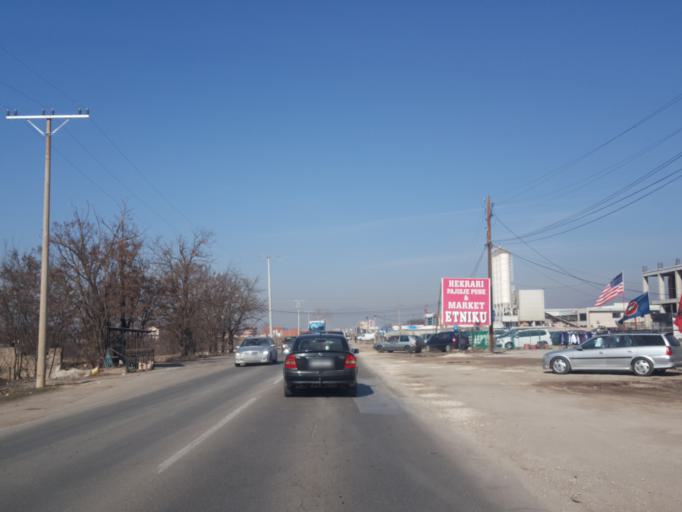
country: XK
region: Mitrovica
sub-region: Vushtrri
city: Vushtrri
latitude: 42.7988
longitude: 20.9969
